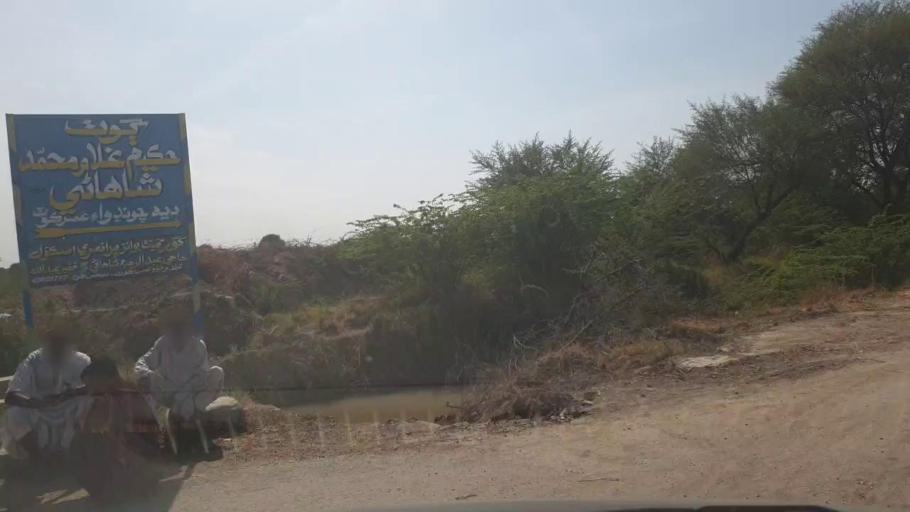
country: PK
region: Sindh
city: Kunri
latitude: 25.1850
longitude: 69.6771
